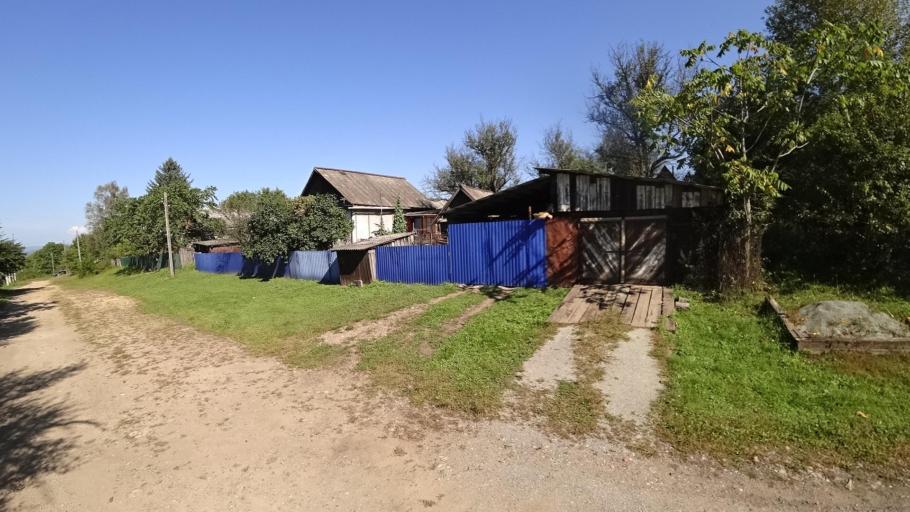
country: RU
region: Jewish Autonomous Oblast
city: Bira
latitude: 49.0049
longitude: 132.4692
